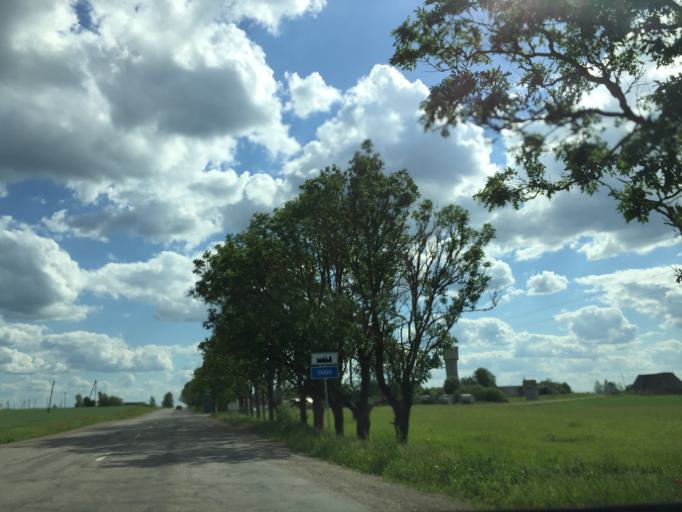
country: LV
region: Jaunpils
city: Jaunpils
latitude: 56.8445
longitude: 23.0419
